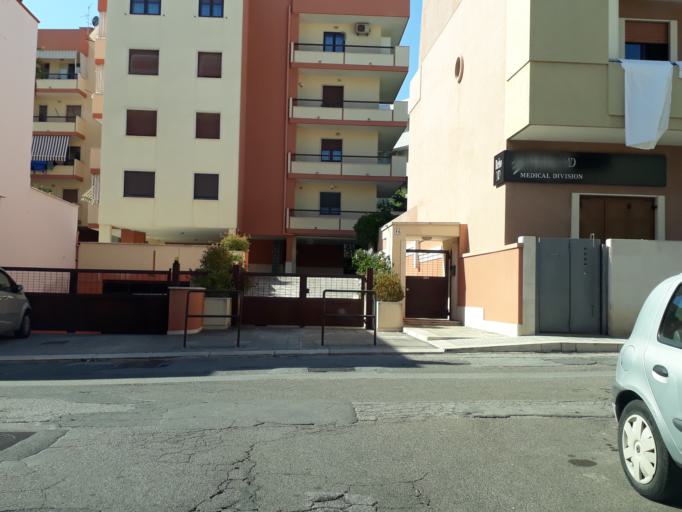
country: IT
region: Apulia
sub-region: Provincia di Bari
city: Monopoli
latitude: 40.9501
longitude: 17.2947
